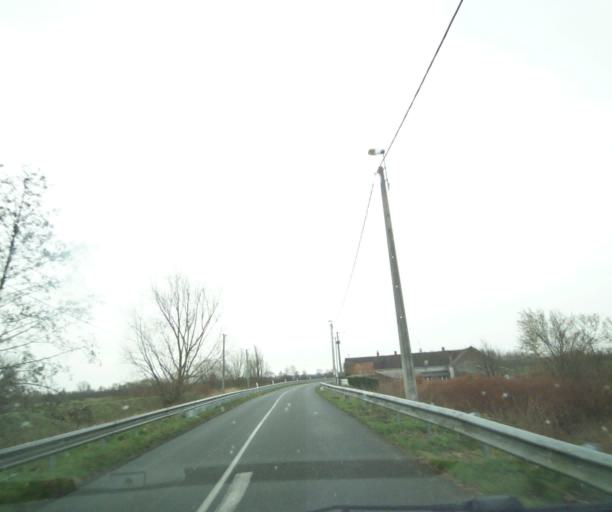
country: FR
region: Nord-Pas-de-Calais
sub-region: Departement du Nord
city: Crespin
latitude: 50.4360
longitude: 3.6434
